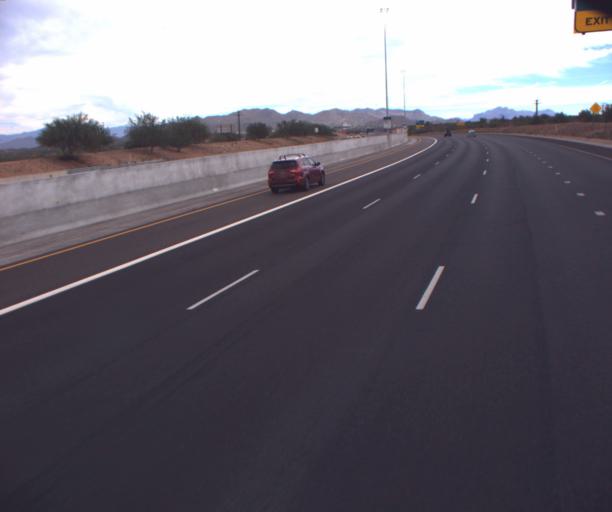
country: US
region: Arizona
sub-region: Maricopa County
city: Mesa
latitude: 33.4803
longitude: -111.7471
